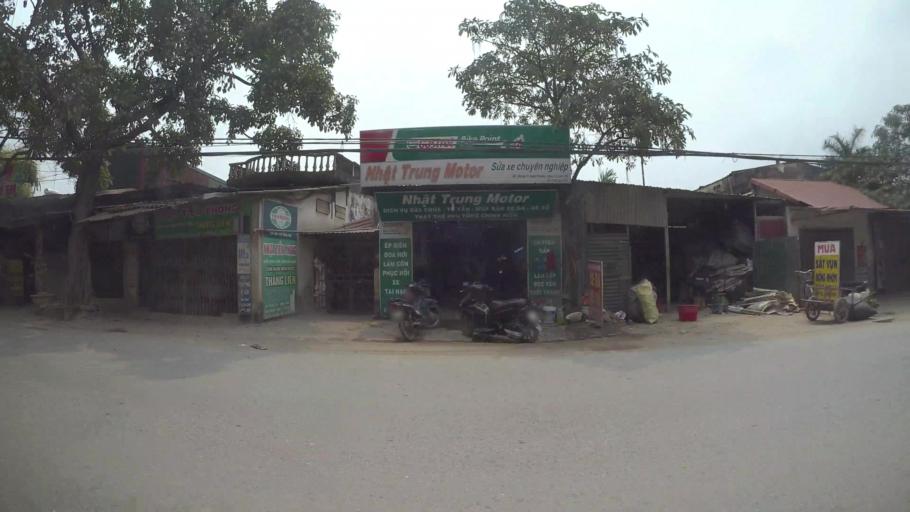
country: VN
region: Ha Noi
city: Cau Dien
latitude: 21.0320
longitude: 105.7392
